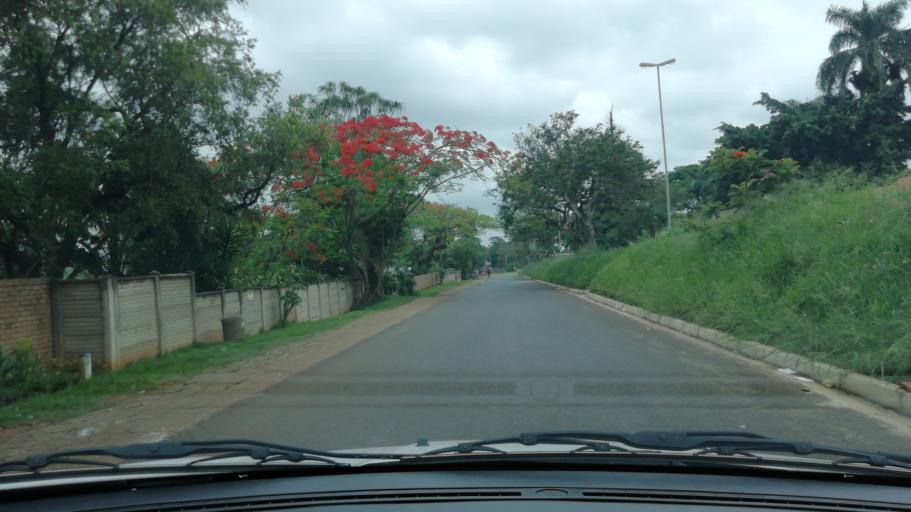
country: ZA
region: KwaZulu-Natal
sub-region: uThungulu District Municipality
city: Empangeni
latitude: -28.7531
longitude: 31.8952
